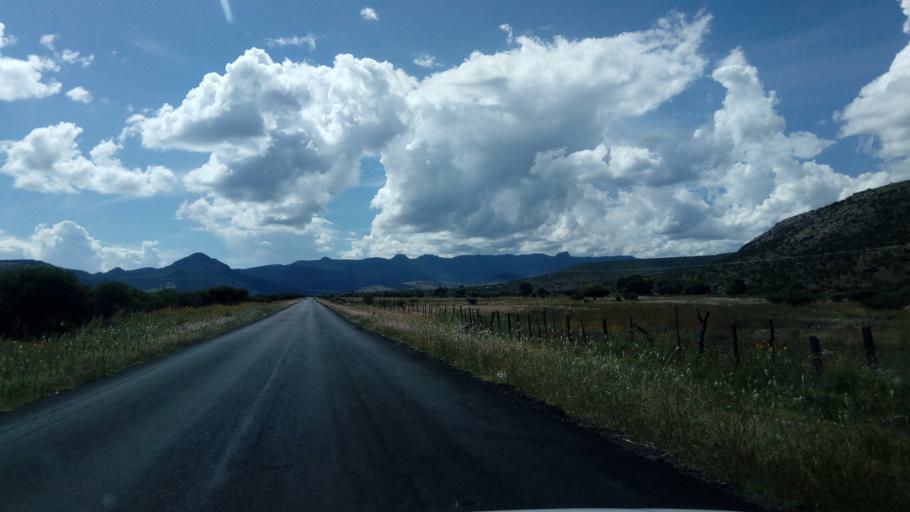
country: MX
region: Durango
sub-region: Durango
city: Jose Refugio Salcido
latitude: 23.8127
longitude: -104.4836
